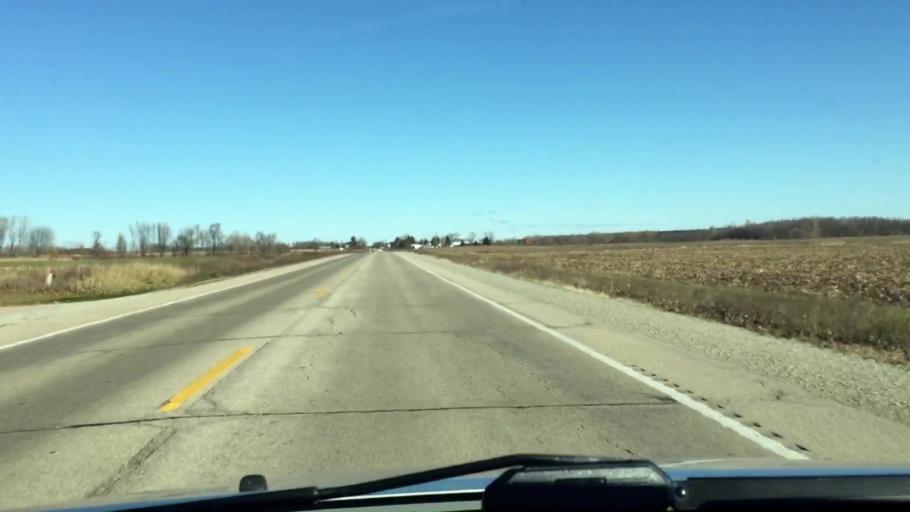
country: US
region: Wisconsin
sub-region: Brown County
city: Pulaski
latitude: 44.6305
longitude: -88.2202
